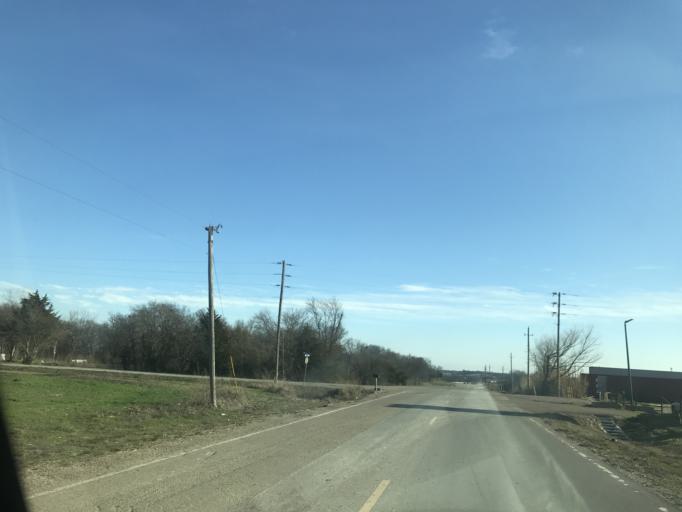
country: US
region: Texas
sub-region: Dallas County
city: Wilmer
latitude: 32.5664
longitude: -96.6694
